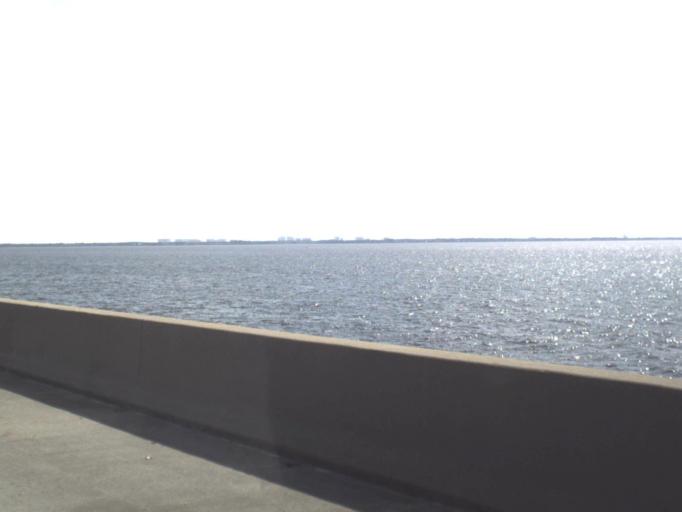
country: US
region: Florida
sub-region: Walton County
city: Miramar Beach
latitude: 30.4461
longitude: -86.4160
